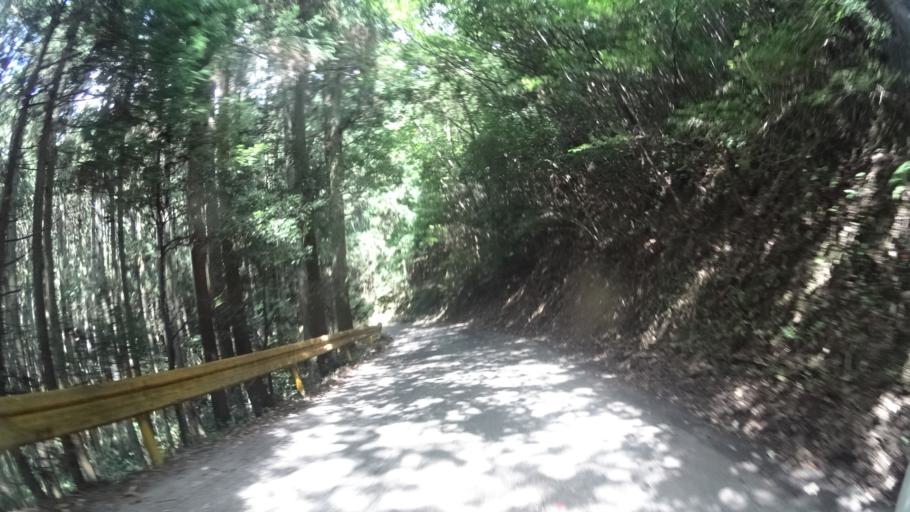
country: JP
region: Yamaguchi
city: Hagi
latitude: 34.4940
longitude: 131.5653
